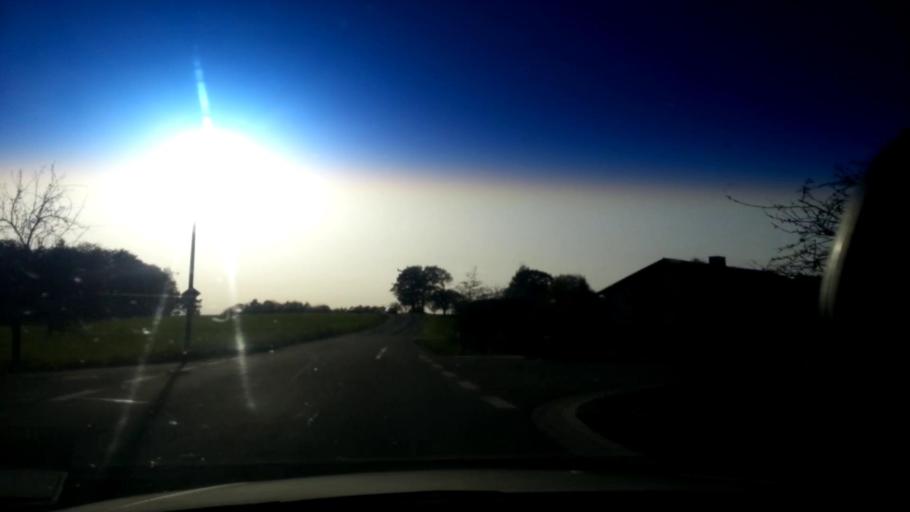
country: DE
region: Bavaria
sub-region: Upper Franconia
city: Poxdorf
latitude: 49.9626
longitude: 11.0980
